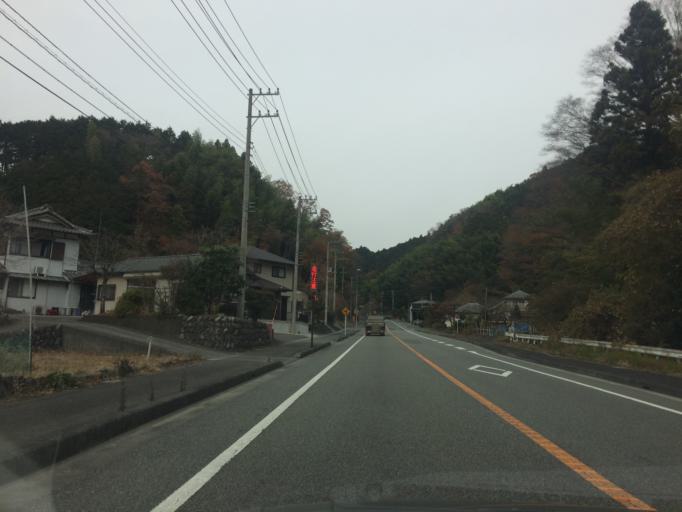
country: JP
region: Shizuoka
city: Fujinomiya
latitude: 35.2646
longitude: 138.4623
